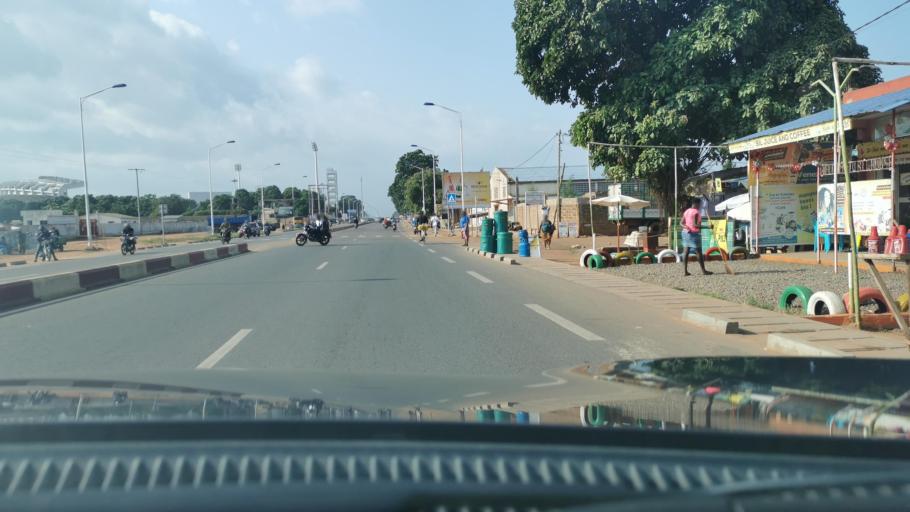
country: TG
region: Maritime
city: Lome
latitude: 6.1969
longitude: 1.2393
